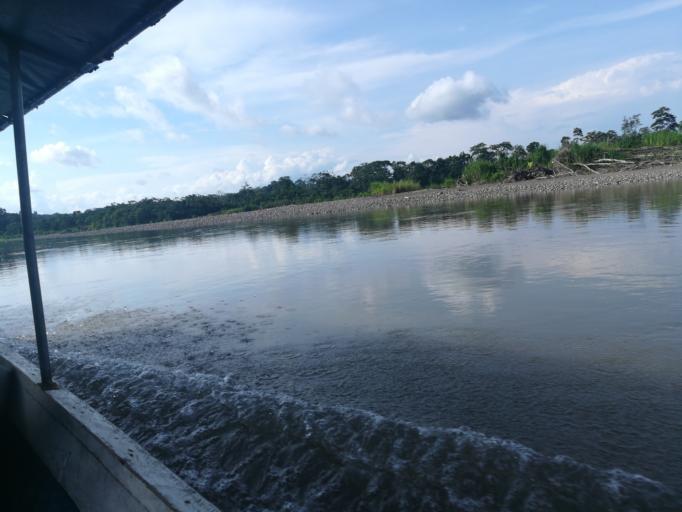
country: EC
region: Orellana
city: Boca Suno
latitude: -0.8508
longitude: -77.2097
